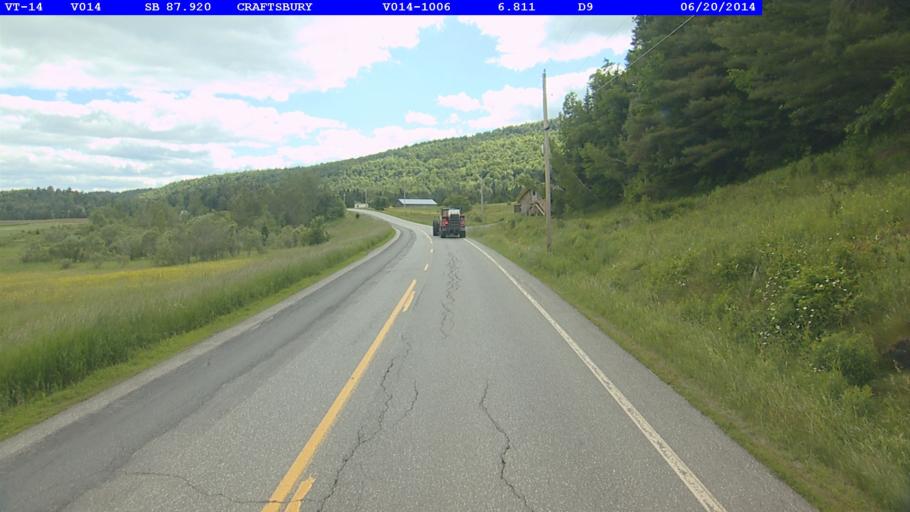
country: US
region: Vermont
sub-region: Caledonia County
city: Hardwick
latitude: 44.6879
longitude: -72.4005
